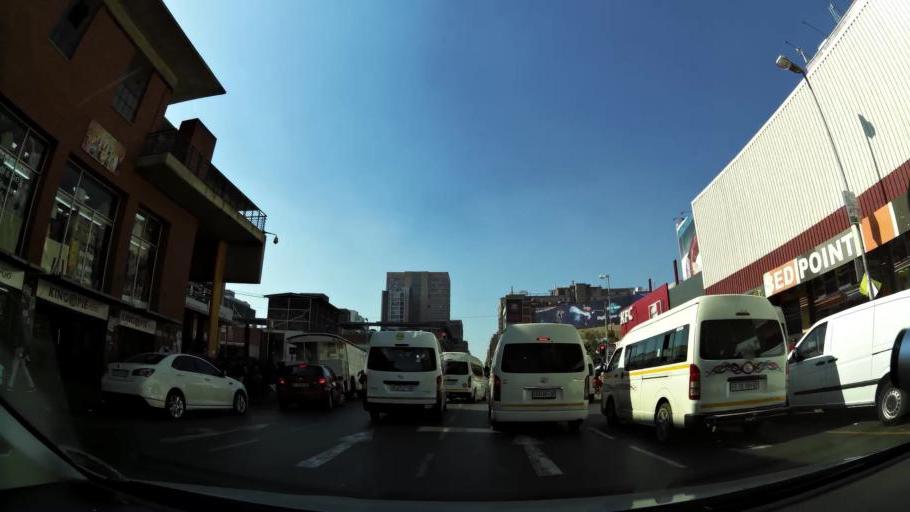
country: ZA
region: Gauteng
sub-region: City of Johannesburg Metropolitan Municipality
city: Johannesburg
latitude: -26.2014
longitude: 28.0370
